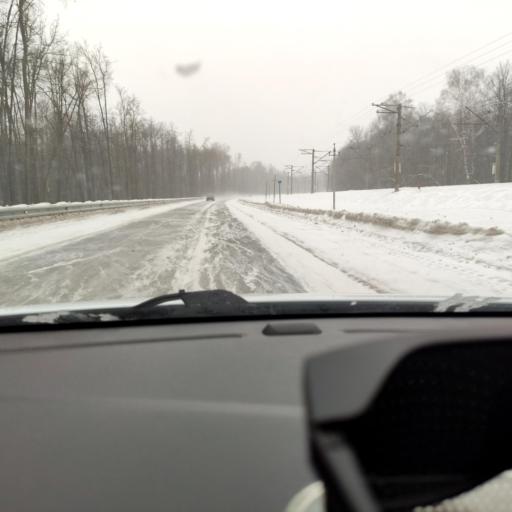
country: RU
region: Tatarstan
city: Vysokaya Gora
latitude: 55.9197
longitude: 49.2825
